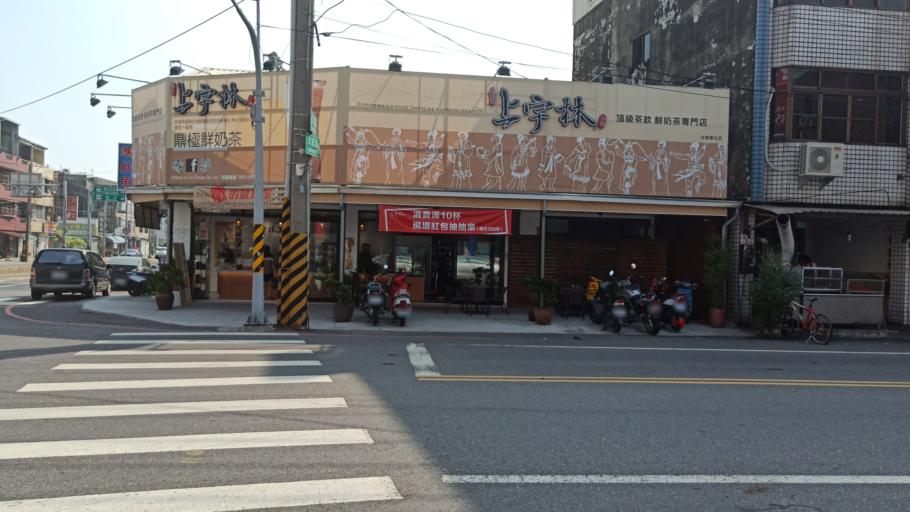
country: TW
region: Taiwan
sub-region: Tainan
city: Tainan
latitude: 23.1291
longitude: 120.2940
